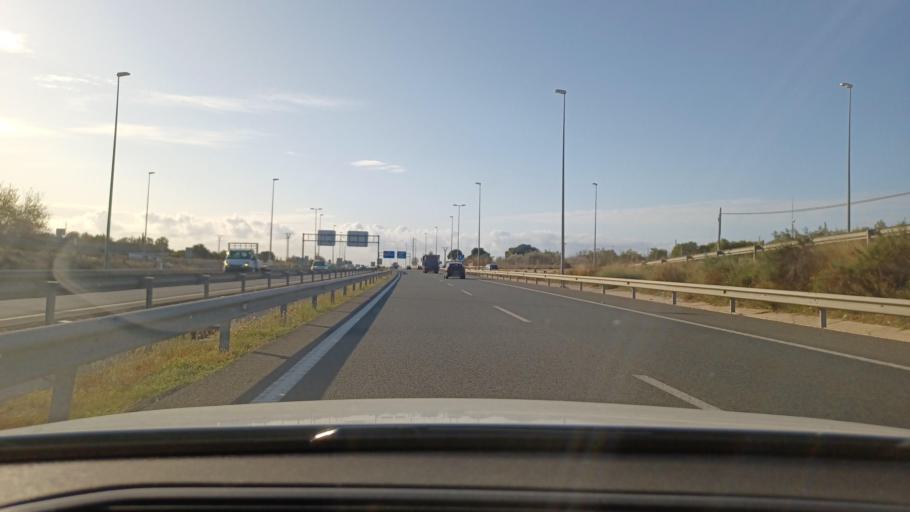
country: ES
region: Valencia
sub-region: Provincia de Alicante
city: Elche
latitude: 38.2850
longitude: -0.6648
